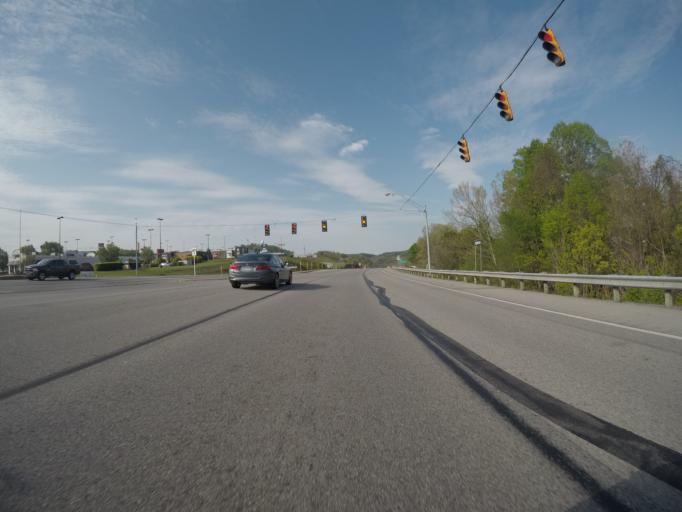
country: US
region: West Virginia
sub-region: Kanawha County
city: Dunbar
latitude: 38.3206
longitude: -81.7177
